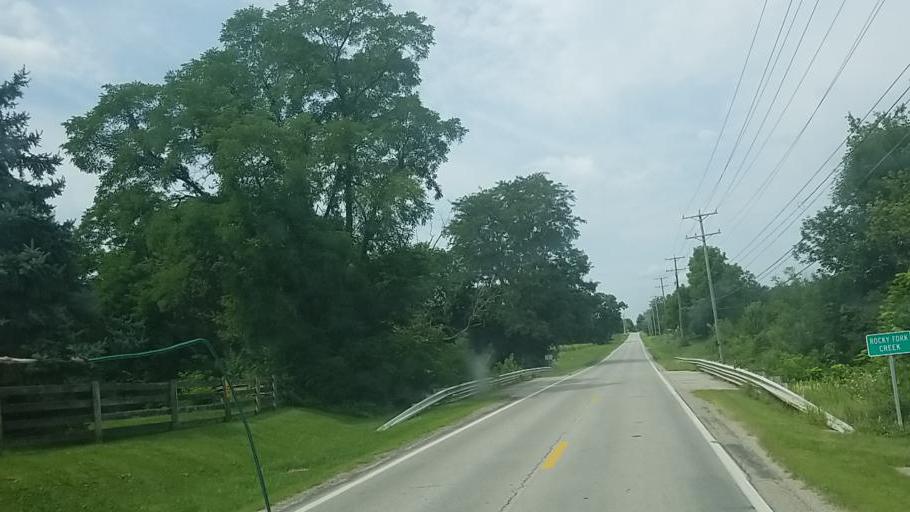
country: US
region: Ohio
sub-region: Franklin County
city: New Albany
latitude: 40.1138
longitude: -82.8312
